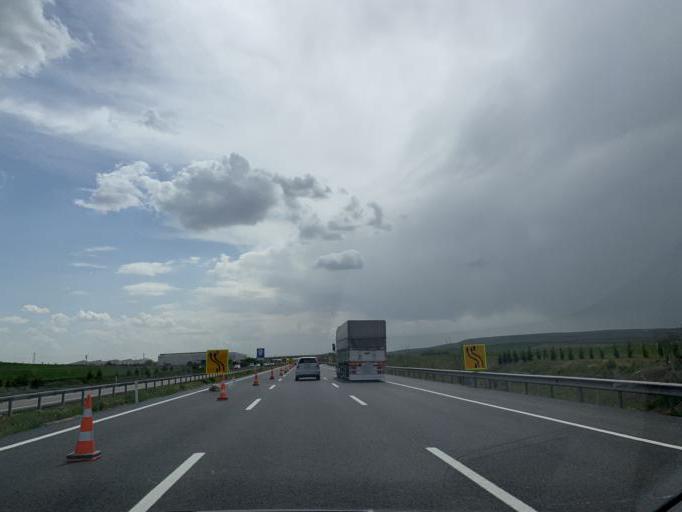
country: TR
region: Ankara
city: Polatli
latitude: 39.6555
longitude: 32.2177
